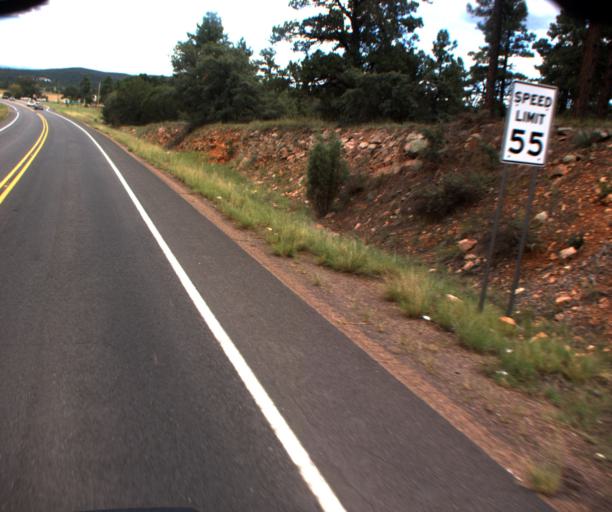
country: US
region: Arizona
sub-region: Navajo County
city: Linden
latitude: 34.2873
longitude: -110.1721
